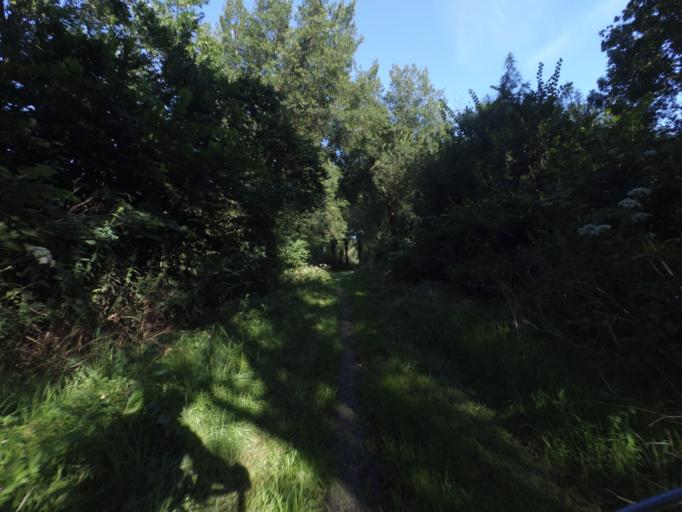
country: NL
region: Flevoland
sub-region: Gemeente Zeewolde
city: Zeewolde
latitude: 52.3961
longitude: 5.4929
